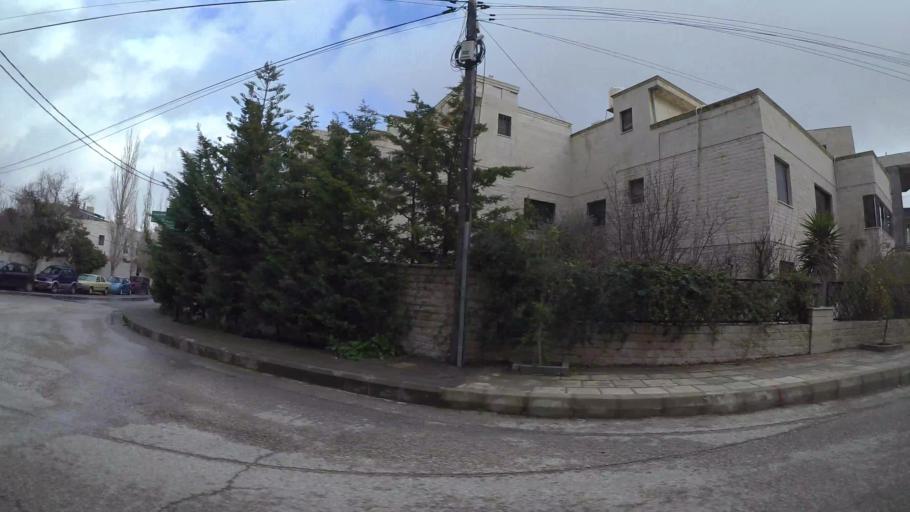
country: JO
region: Amman
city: Wadi as Sir
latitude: 31.9500
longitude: 35.8763
